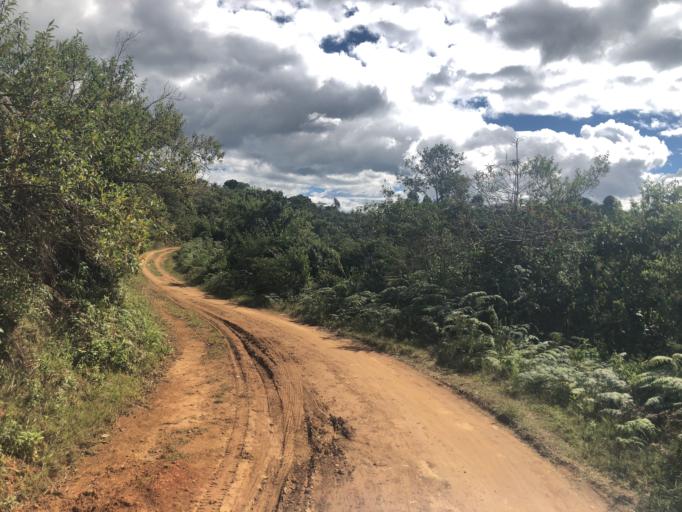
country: CO
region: Cauca
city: Silvia
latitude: 2.6787
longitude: -76.4400
